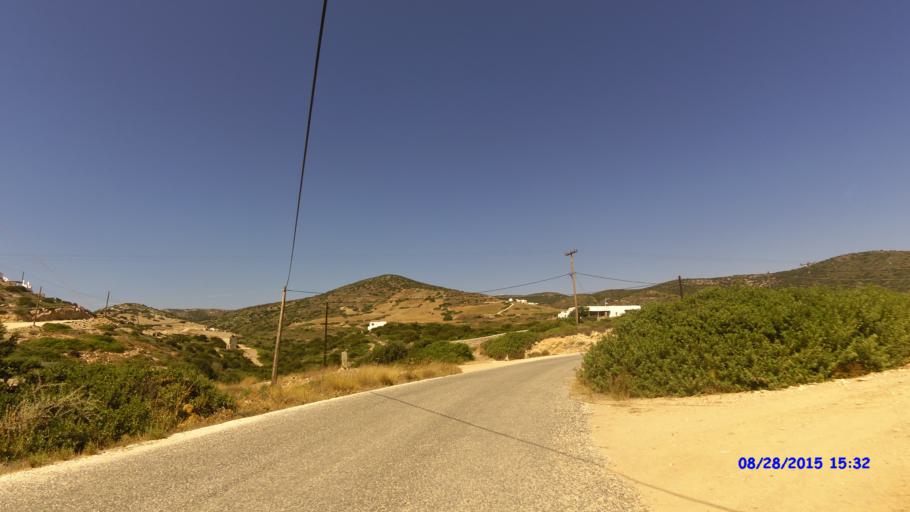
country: GR
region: South Aegean
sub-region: Nomos Kykladon
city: Antiparos
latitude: 36.9793
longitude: 25.0283
